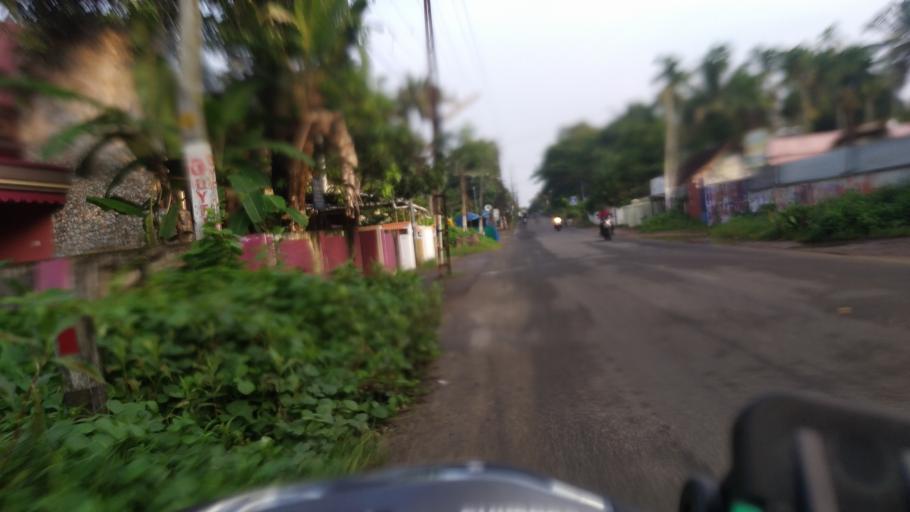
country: IN
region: Kerala
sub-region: Ernakulam
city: Elur
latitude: 10.0360
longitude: 76.2204
